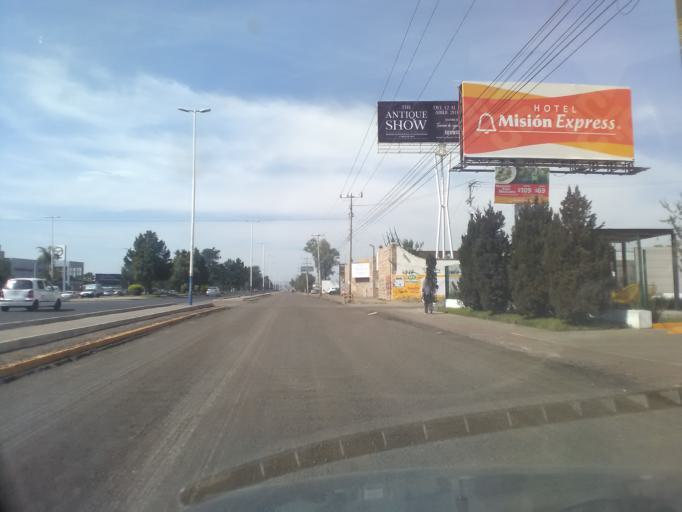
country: MX
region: Durango
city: Victoria de Durango
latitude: 24.0550
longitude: -104.6151
